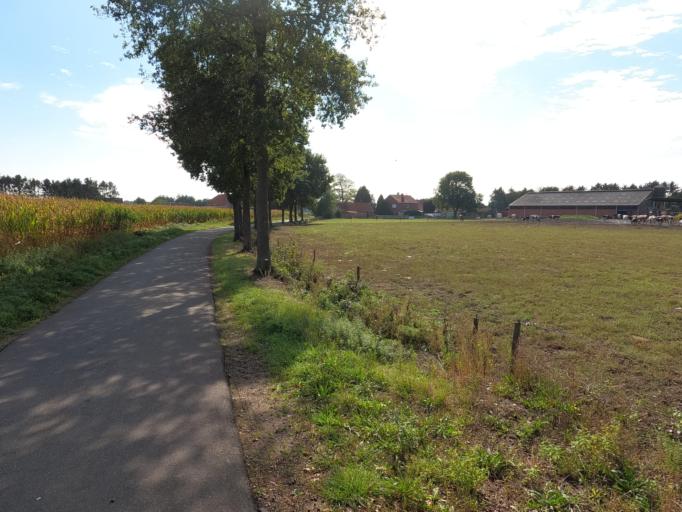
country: BE
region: Flanders
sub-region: Provincie Antwerpen
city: Lille
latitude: 51.2128
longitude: 4.8246
